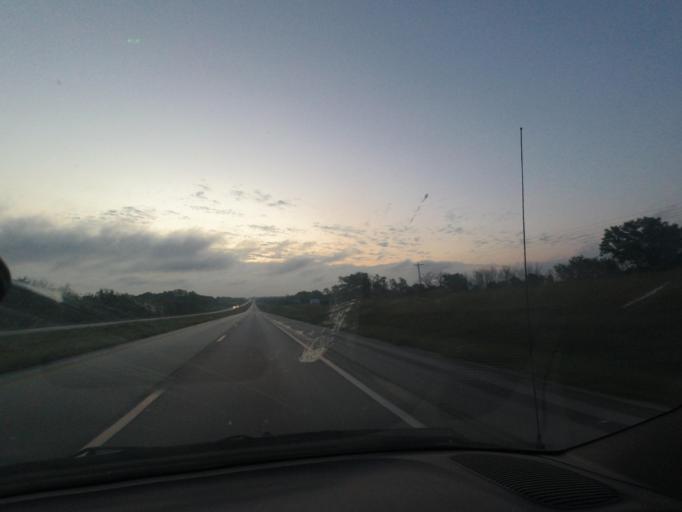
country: US
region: Missouri
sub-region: Linn County
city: Brookfield
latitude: 39.7620
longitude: -93.0031
